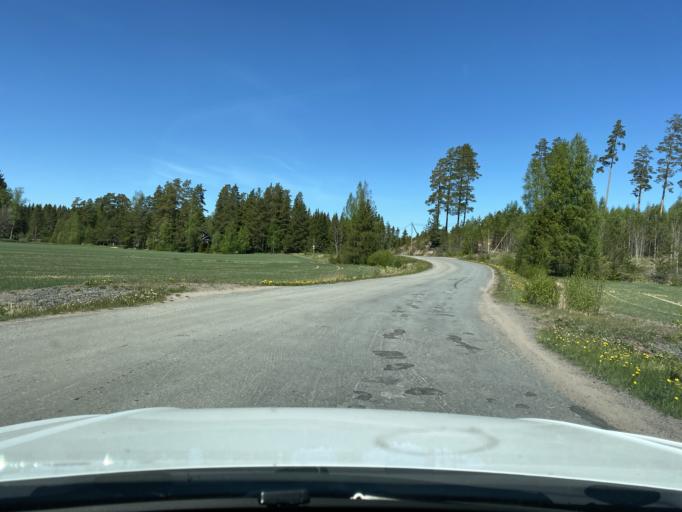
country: FI
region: Satakunta
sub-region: Rauma
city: Kiukainen
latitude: 61.1311
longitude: 21.9889
